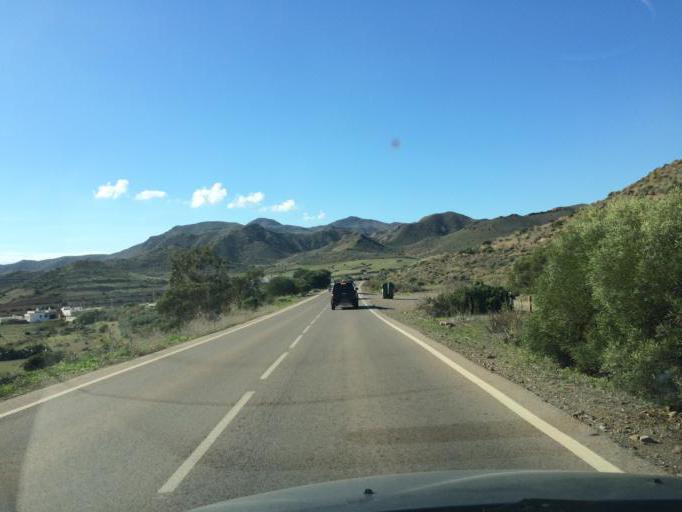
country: ES
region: Andalusia
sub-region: Provincia de Almeria
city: San Jose
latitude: 36.7968
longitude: -2.1071
